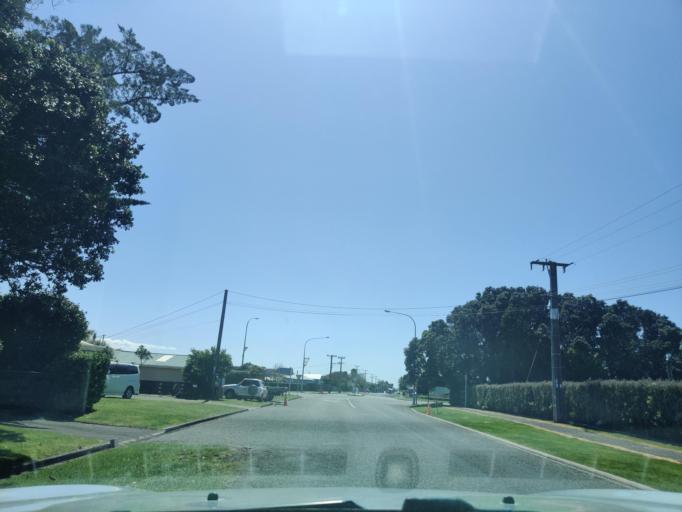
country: NZ
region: Taranaki
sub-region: South Taranaki District
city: Hawera
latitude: -39.5920
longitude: 174.2695
